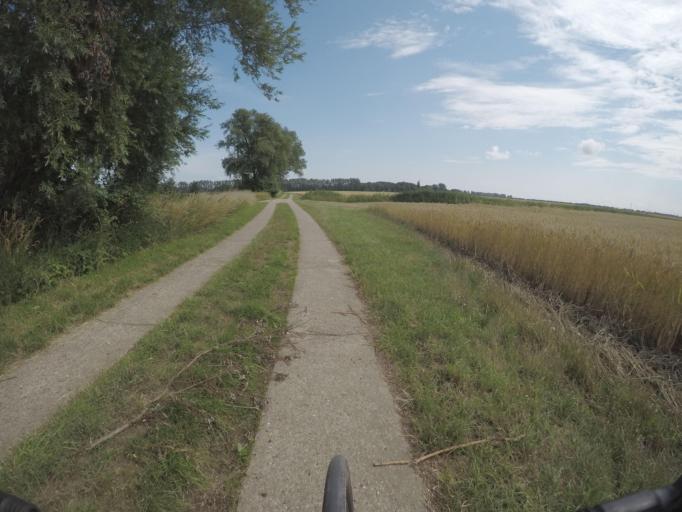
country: DE
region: Mecklenburg-Vorpommern
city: Altefahr
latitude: 54.3684
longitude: 13.1395
